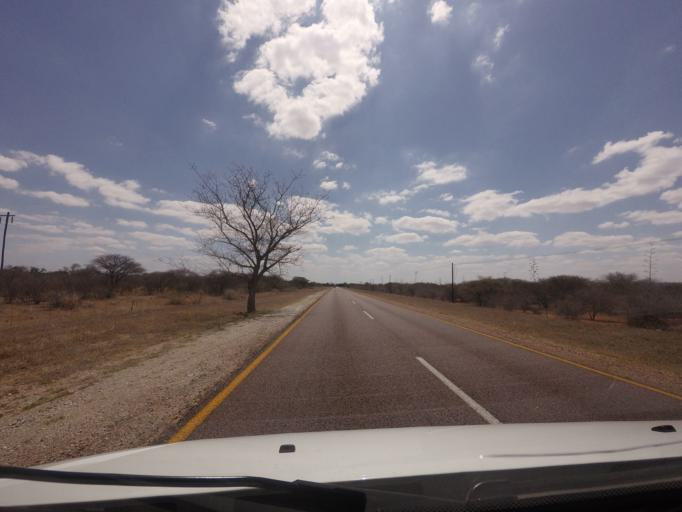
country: ZA
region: Limpopo
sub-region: Capricorn District Municipality
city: Dendron
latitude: -23.5363
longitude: 28.7033
